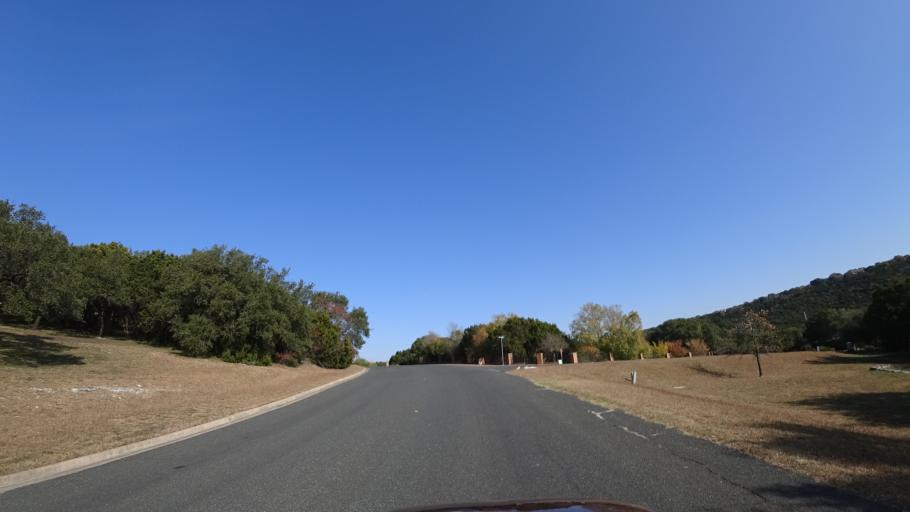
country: US
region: Texas
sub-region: Williamson County
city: Jollyville
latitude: 30.3745
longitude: -97.8086
